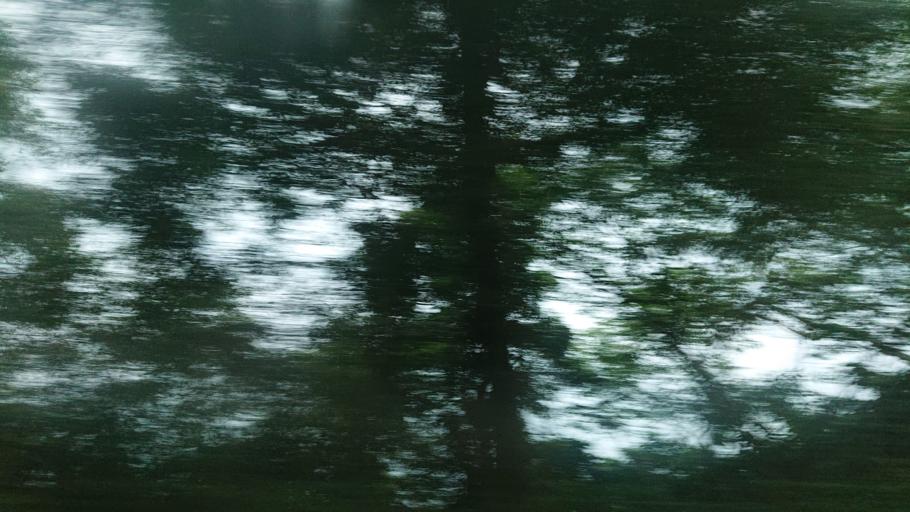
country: TW
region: Taiwan
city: Lugu
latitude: 23.5908
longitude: 120.7127
